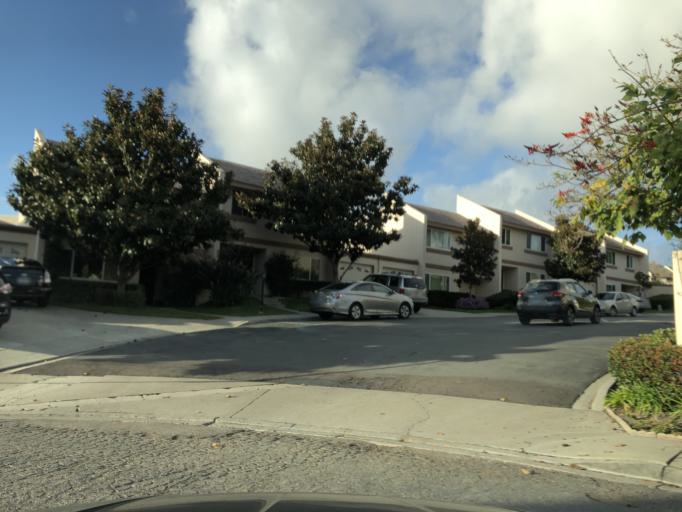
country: US
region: California
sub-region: San Diego County
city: San Diego
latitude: 32.8144
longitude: -117.1784
